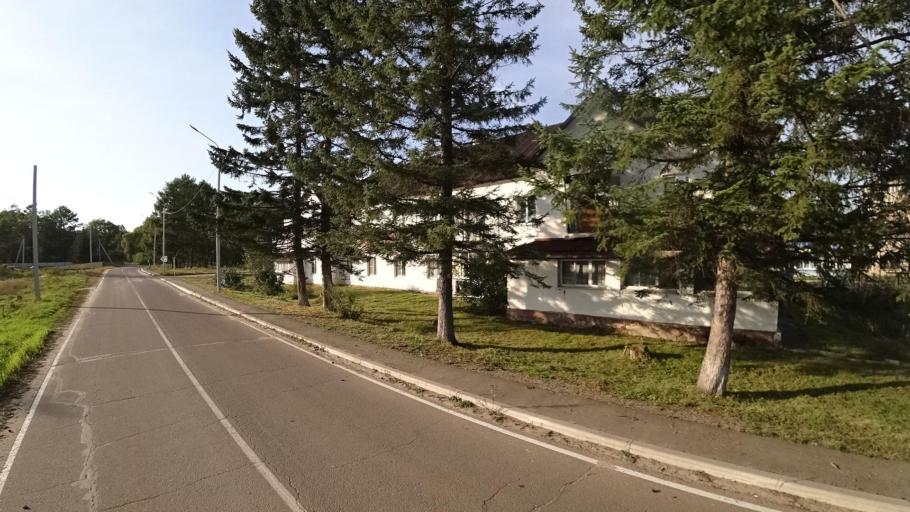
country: RU
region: Jewish Autonomous Oblast
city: Kul'dur
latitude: 49.2030
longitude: 131.6217
